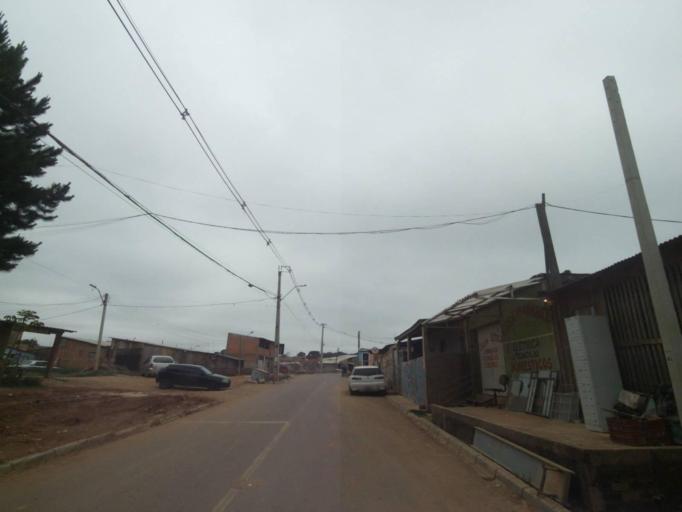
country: BR
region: Parana
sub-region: Araucaria
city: Araucaria
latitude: -25.5079
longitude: -49.3516
